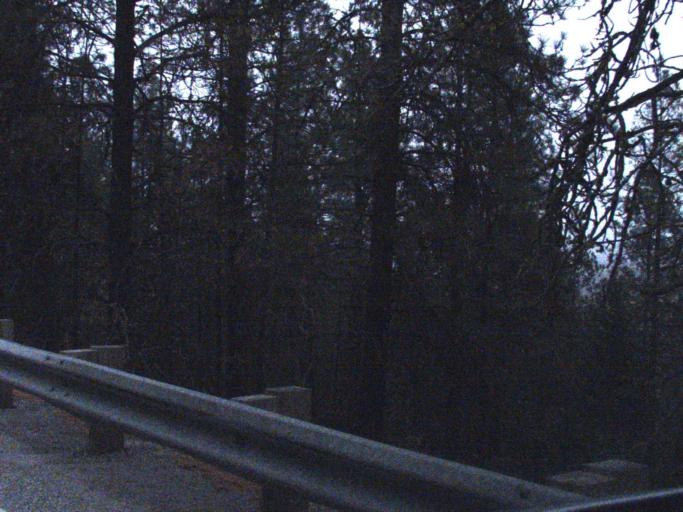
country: US
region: Washington
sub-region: Stevens County
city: Kettle Falls
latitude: 48.7282
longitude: -118.1295
